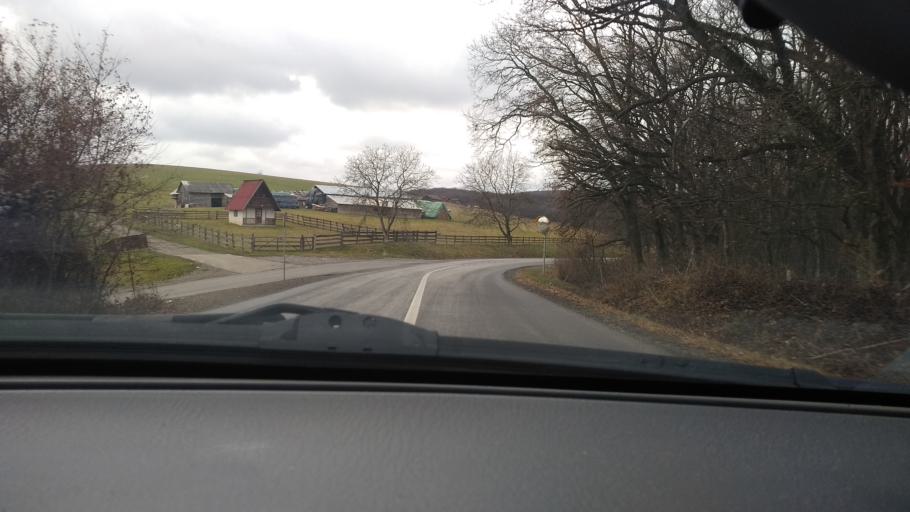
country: RO
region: Mures
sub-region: Comuna Galesti
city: Galesti
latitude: 46.5317
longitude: 24.7062
